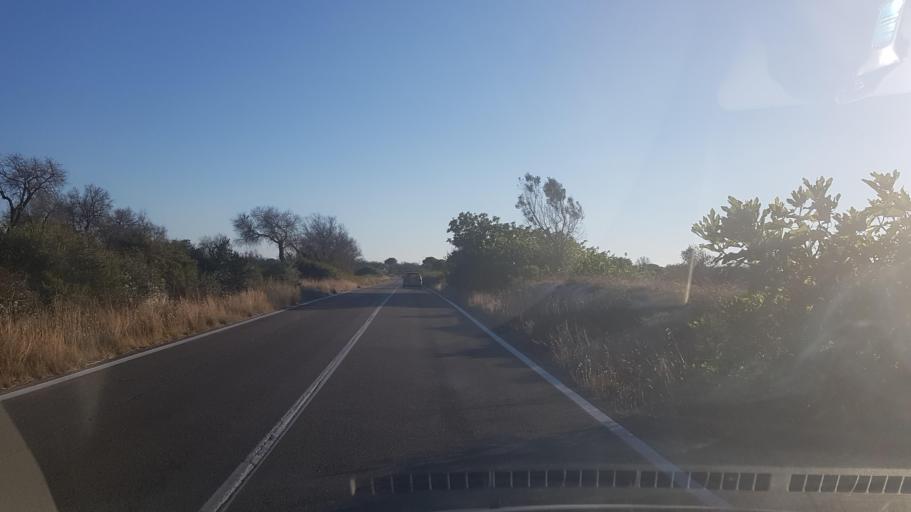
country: IT
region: Apulia
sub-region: Provincia di Lecce
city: Vernole
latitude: 40.3257
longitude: 18.3305
